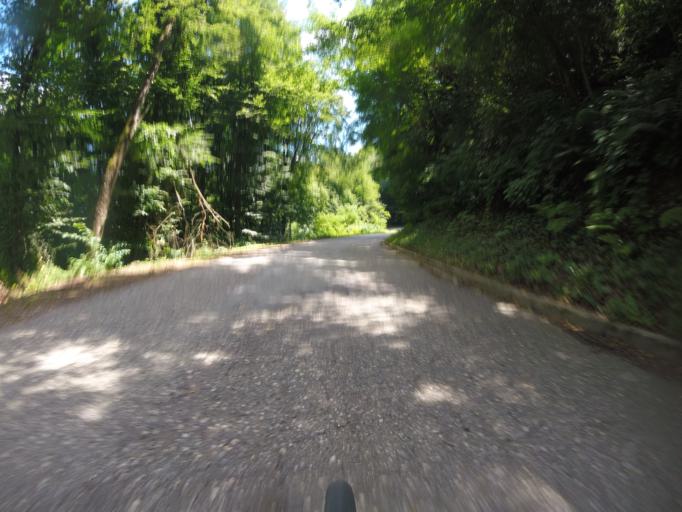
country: HR
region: Karlovacka
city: Ozalj
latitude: 45.6716
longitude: 15.4673
